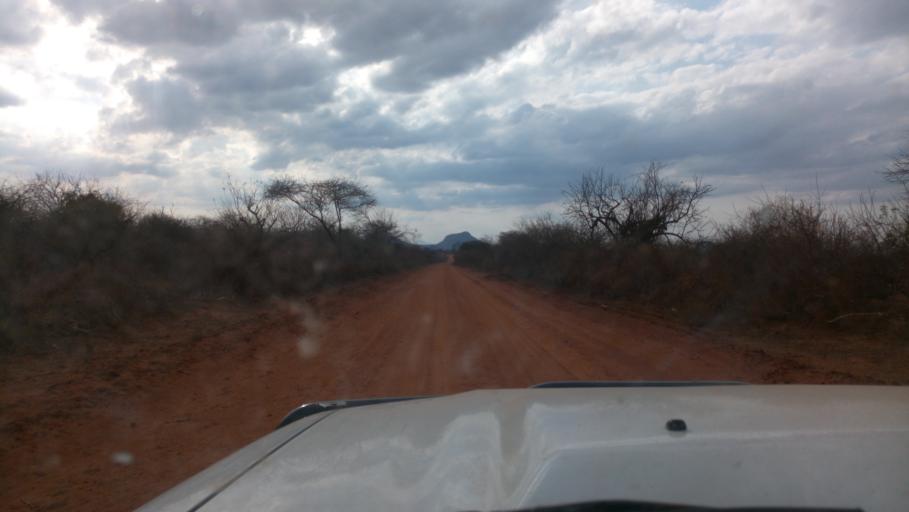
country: KE
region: Kitui
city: Kitui
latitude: -1.7434
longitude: 38.4067
